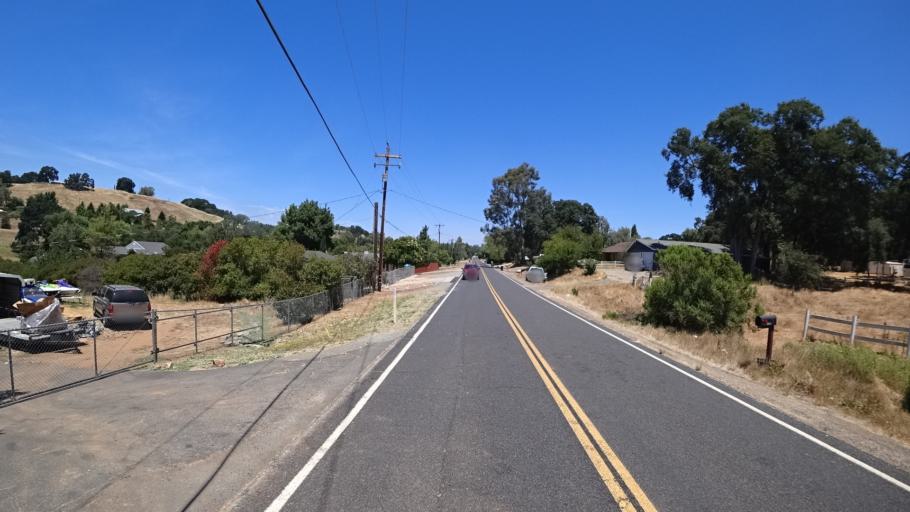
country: US
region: California
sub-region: Calaveras County
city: Rancho Calaveras
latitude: 38.1107
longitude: -120.8666
